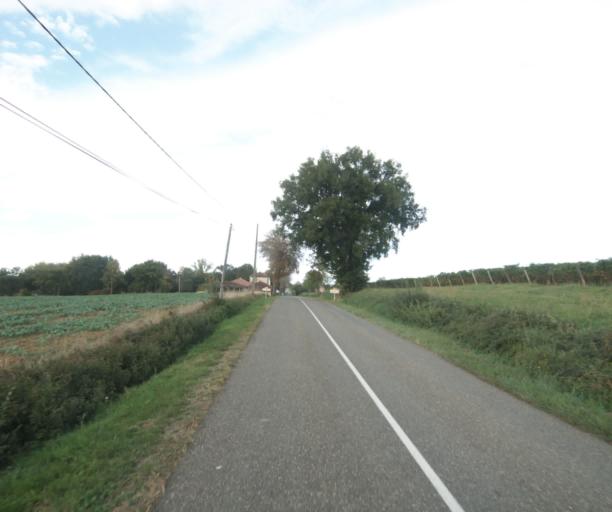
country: FR
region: Midi-Pyrenees
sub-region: Departement du Gers
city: Le Houga
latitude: 43.8454
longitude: -0.1359
